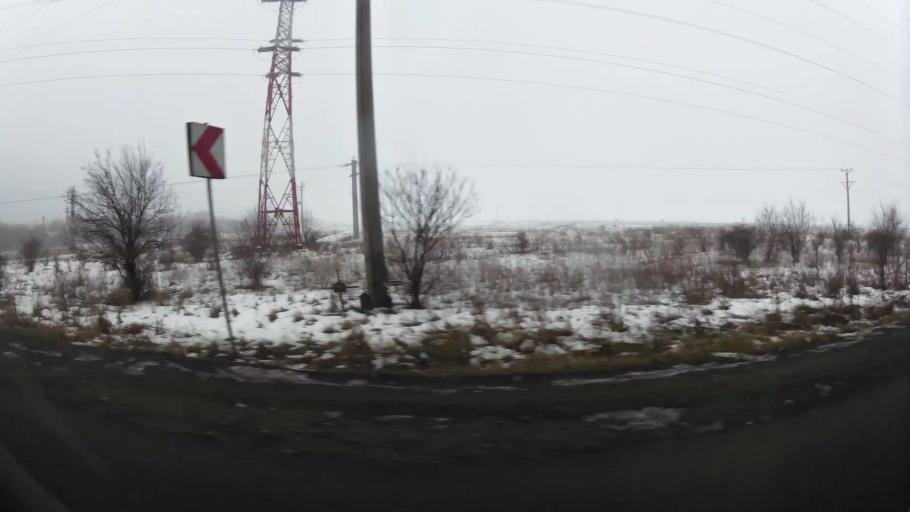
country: RO
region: Ilfov
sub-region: Comuna Clinceni
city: Olteni
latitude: 44.4228
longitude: 25.9680
